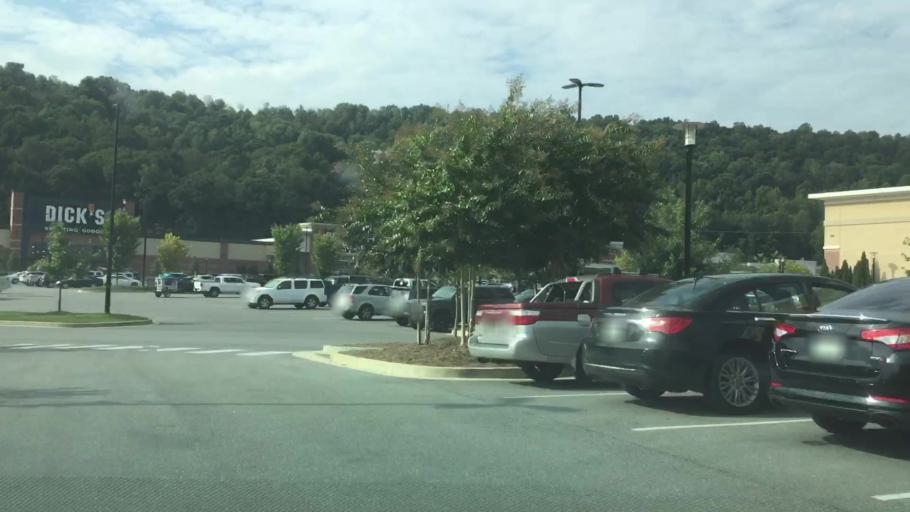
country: US
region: Tennessee
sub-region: Sullivan County
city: Walnut Hill
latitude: 36.5918
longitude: -82.2613
